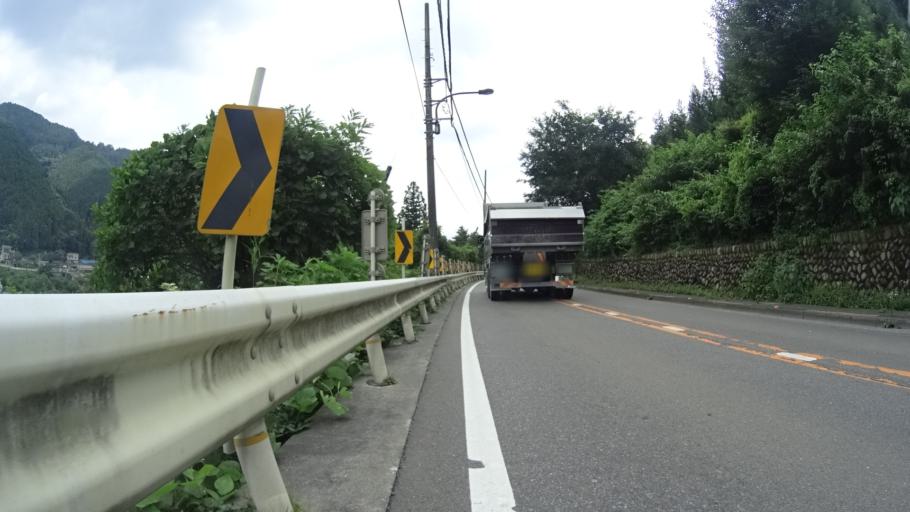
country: JP
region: Tokyo
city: Ome
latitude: 35.8041
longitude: 139.1885
